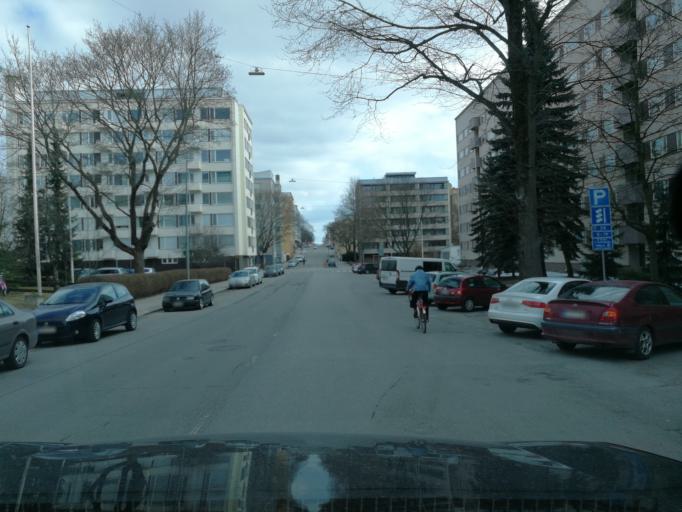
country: FI
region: Varsinais-Suomi
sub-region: Turku
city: Turku
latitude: 60.4437
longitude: 22.2710
